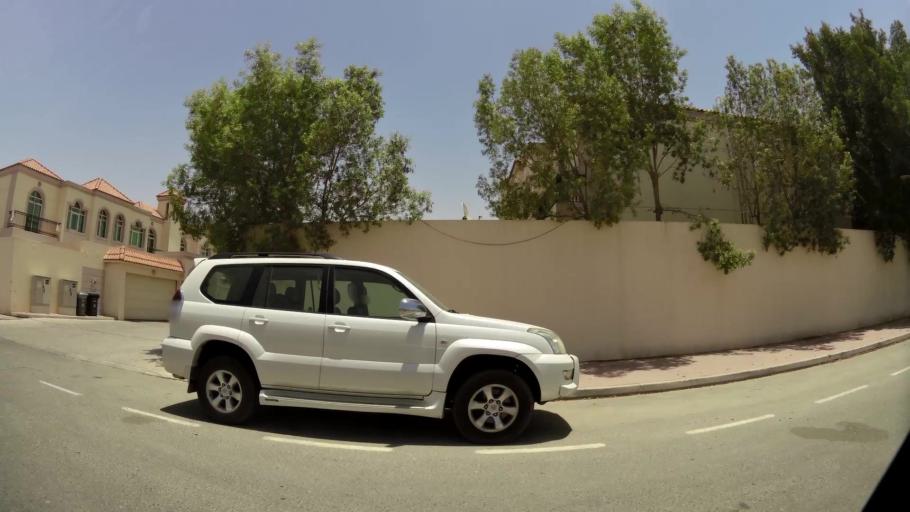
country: AE
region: Dubai
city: Dubai
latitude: 25.1719
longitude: 55.2400
